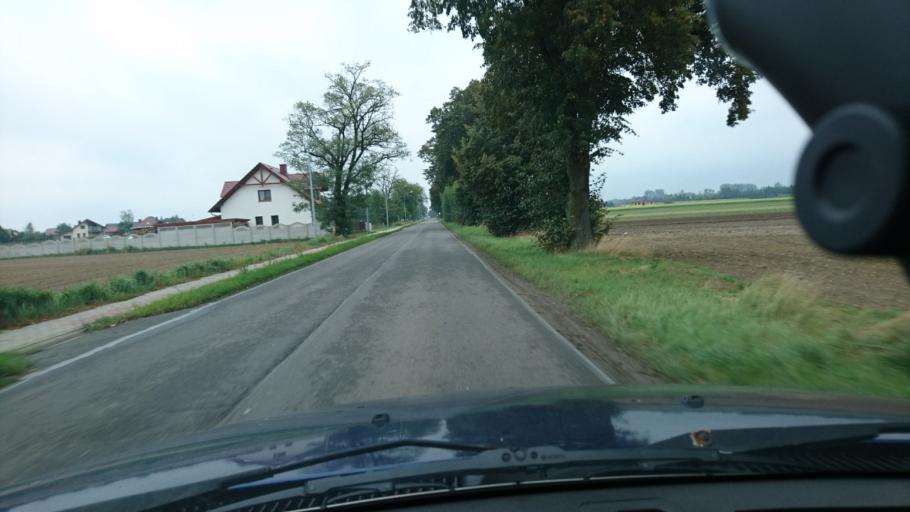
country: PL
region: Greater Poland Voivodeship
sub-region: Powiat ostrowski
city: Odolanow
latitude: 51.5760
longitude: 17.6475
